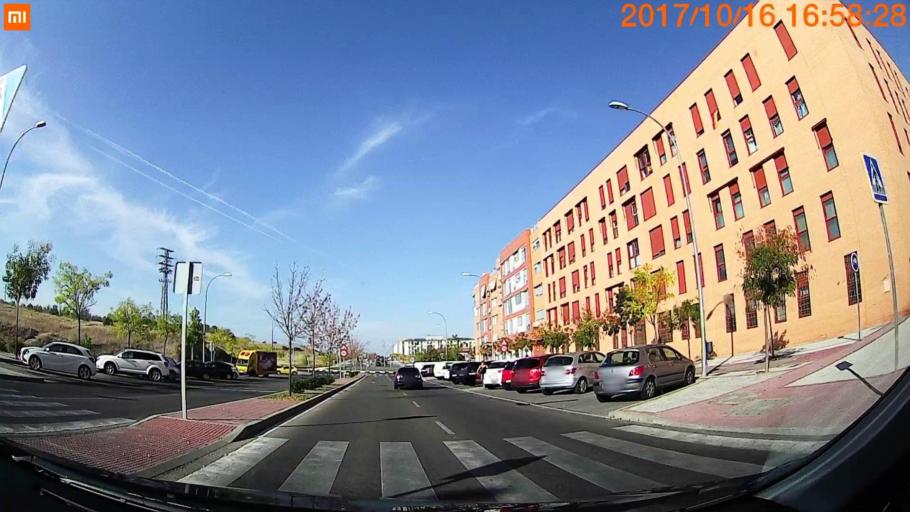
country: ES
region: Madrid
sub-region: Provincia de Madrid
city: Alcobendas
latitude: 40.5517
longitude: -3.6622
